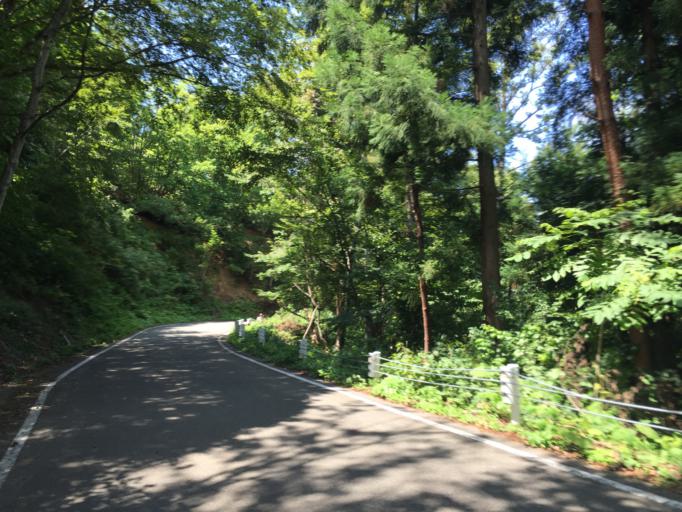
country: JP
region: Fukushima
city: Inawashiro
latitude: 37.4733
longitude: 140.0438
